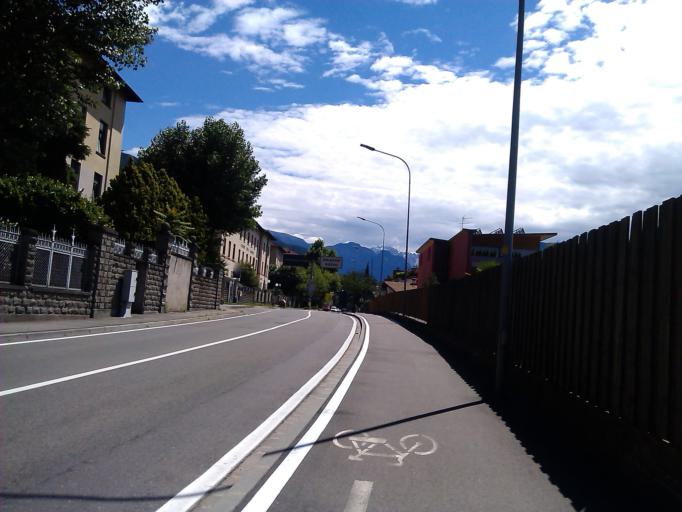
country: IT
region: Trentino-Alto Adige
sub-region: Bolzano
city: Bolzano
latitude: 46.5032
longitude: 11.3240
